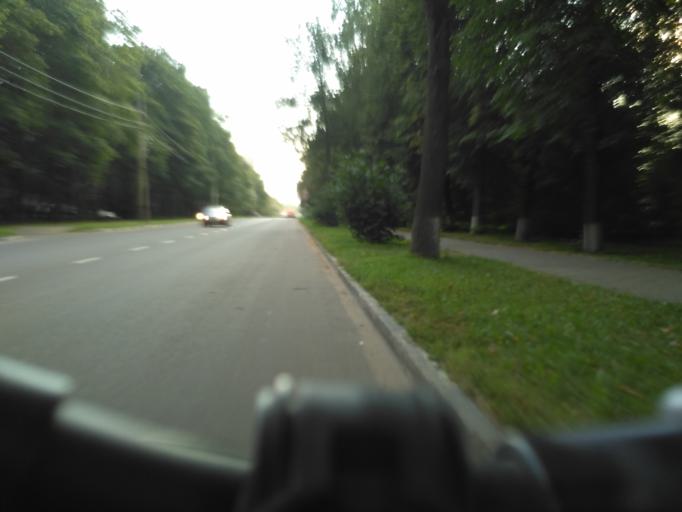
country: RU
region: Moskovskaya
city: Dubna
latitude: 56.7470
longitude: 37.1820
